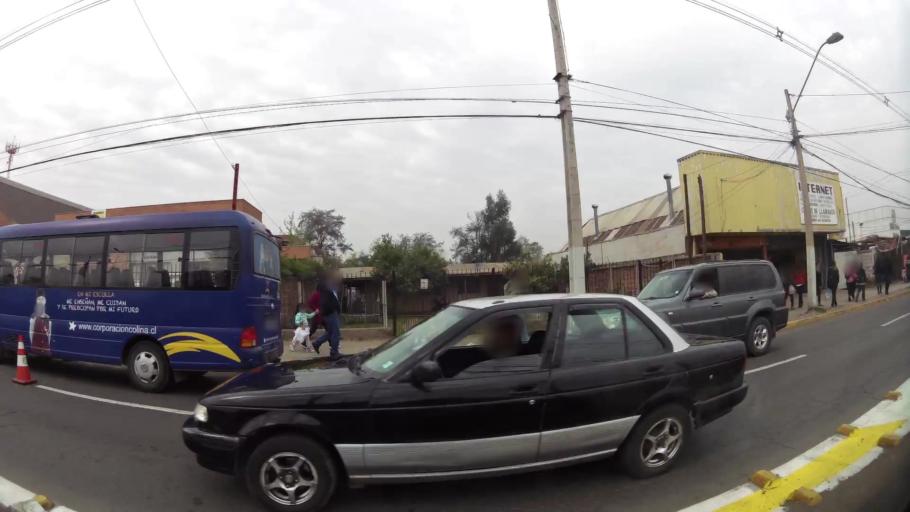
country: CL
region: Santiago Metropolitan
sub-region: Provincia de Chacabuco
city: Chicureo Abajo
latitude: -33.2065
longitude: -70.6774
